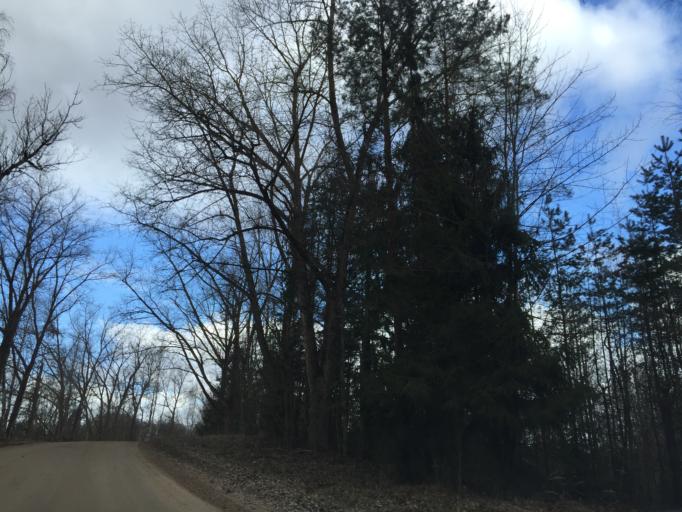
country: LV
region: Akniste
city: Akniste
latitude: 56.0871
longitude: 26.0157
